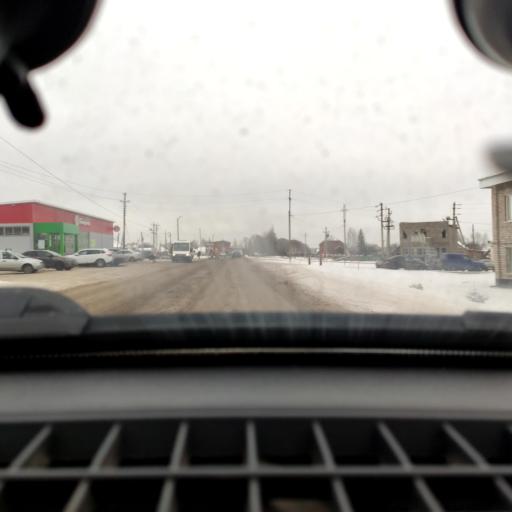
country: RU
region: Bashkortostan
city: Iglino
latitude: 54.8150
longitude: 56.4061
